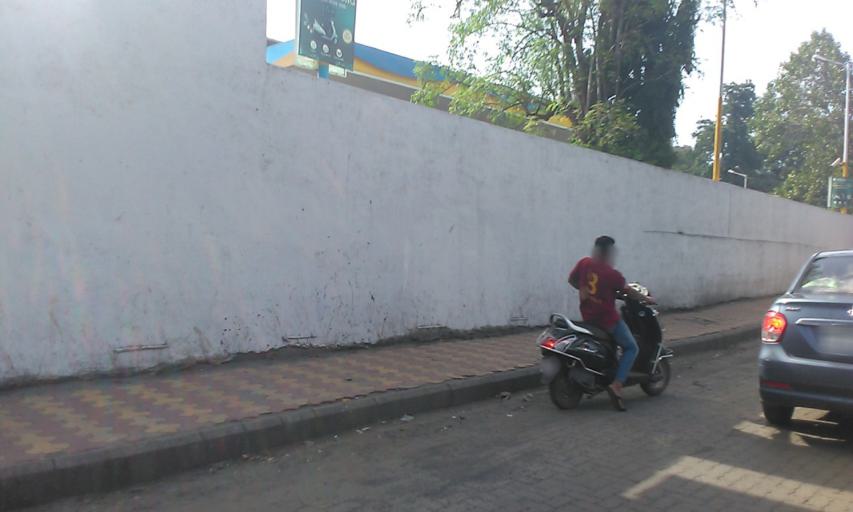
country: IN
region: Maharashtra
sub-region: Pune Division
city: Shivaji Nagar
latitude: 18.5288
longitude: 73.8633
